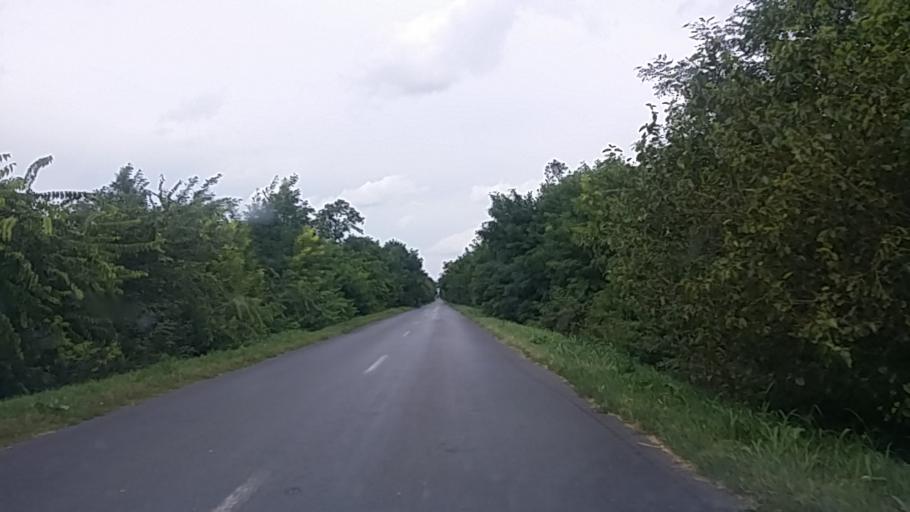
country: HU
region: Tolna
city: Szedres
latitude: 46.5273
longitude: 18.6436
